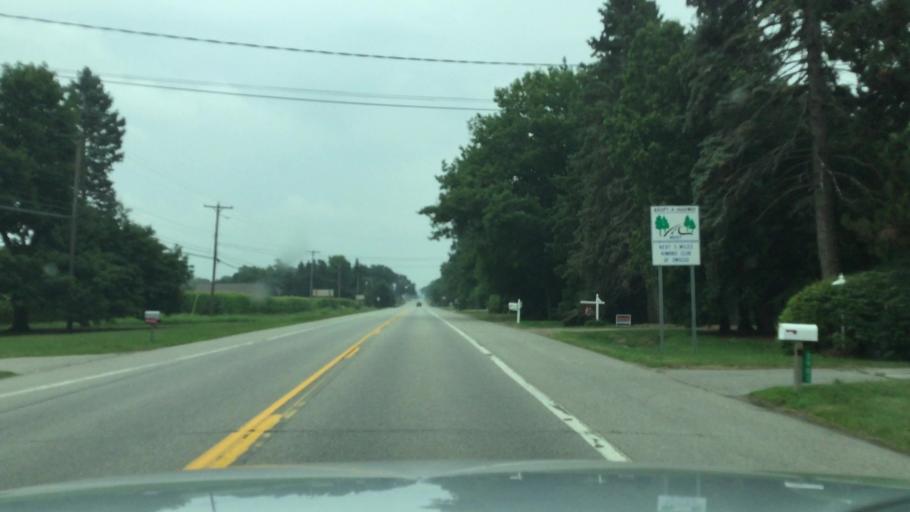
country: US
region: Michigan
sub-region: Shiawassee County
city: New Haven
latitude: 43.0553
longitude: -84.1773
